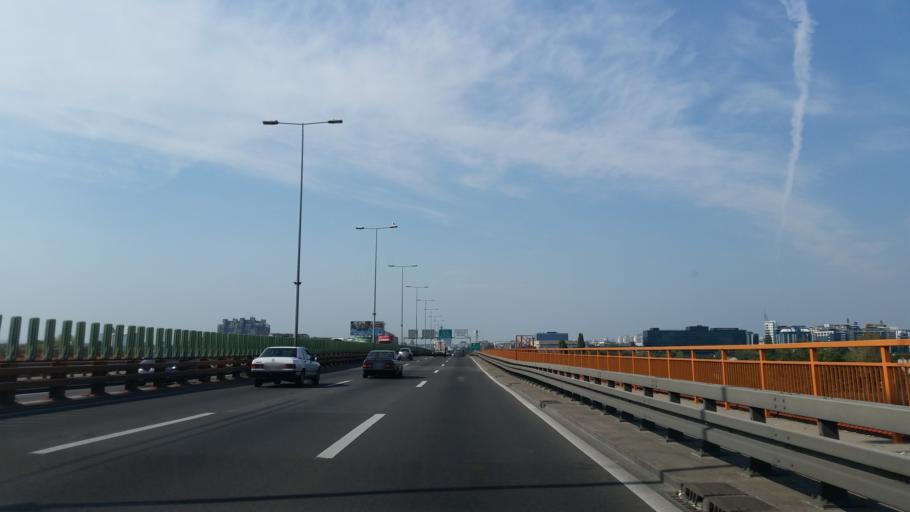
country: RS
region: Central Serbia
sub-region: Belgrade
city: Novi Beograd
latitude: 44.8024
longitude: 20.4417
